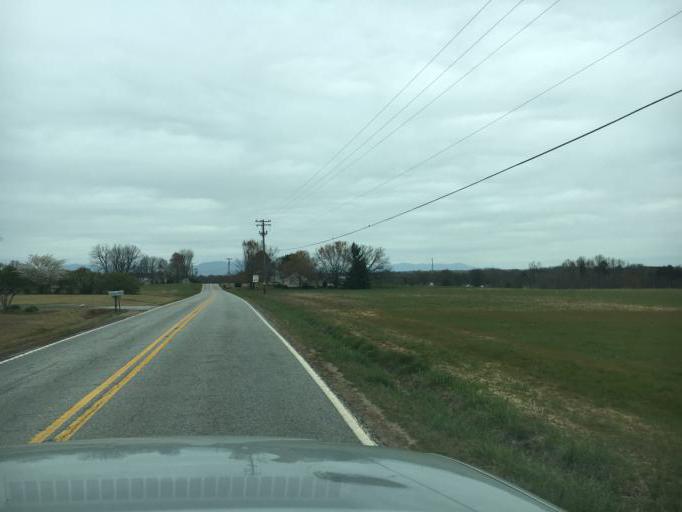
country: US
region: South Carolina
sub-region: Spartanburg County
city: Duncan
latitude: 34.9863
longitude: -82.1722
